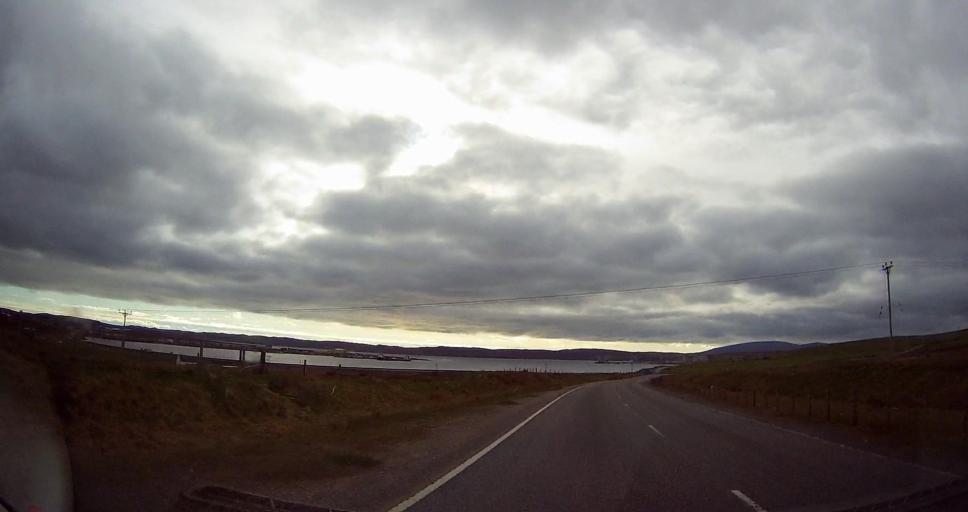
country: GB
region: Scotland
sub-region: Shetland Islands
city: Lerwick
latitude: 60.4455
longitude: -1.2478
